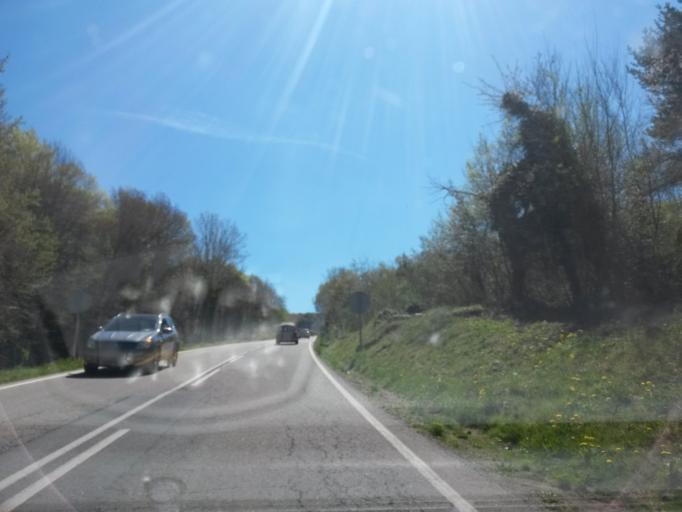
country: ES
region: Catalonia
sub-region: Provincia de Girona
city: Sant Cristofol de les Fonts
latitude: 42.1514
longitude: 2.5259
